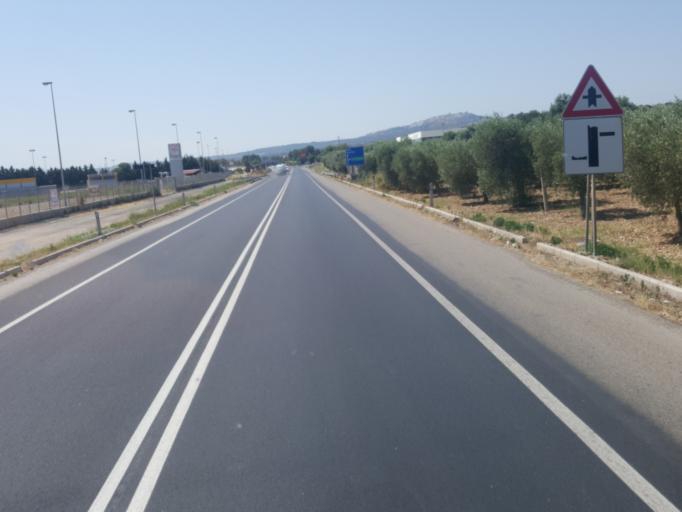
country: IT
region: Apulia
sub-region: Provincia di Taranto
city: Massafra
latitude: 40.5930
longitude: 17.0929
